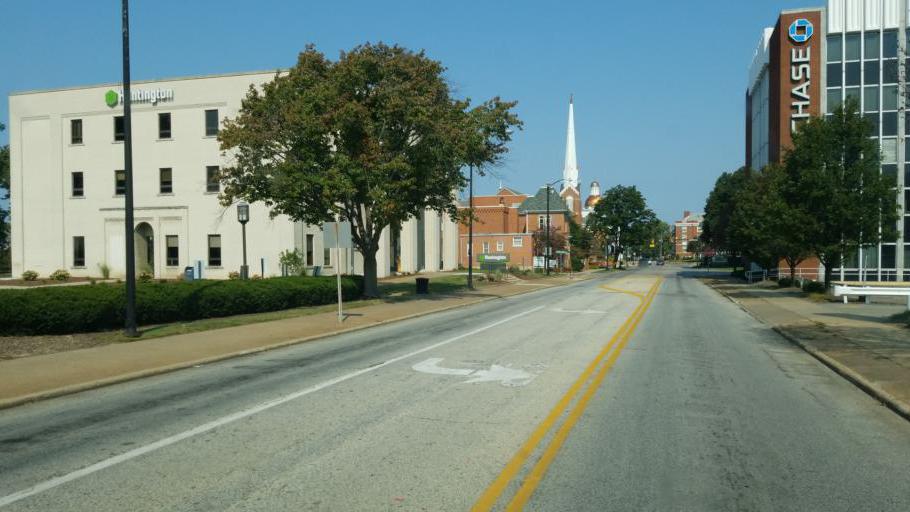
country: US
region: Ohio
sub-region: Lake County
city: Painesville
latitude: 41.7229
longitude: -81.2441
